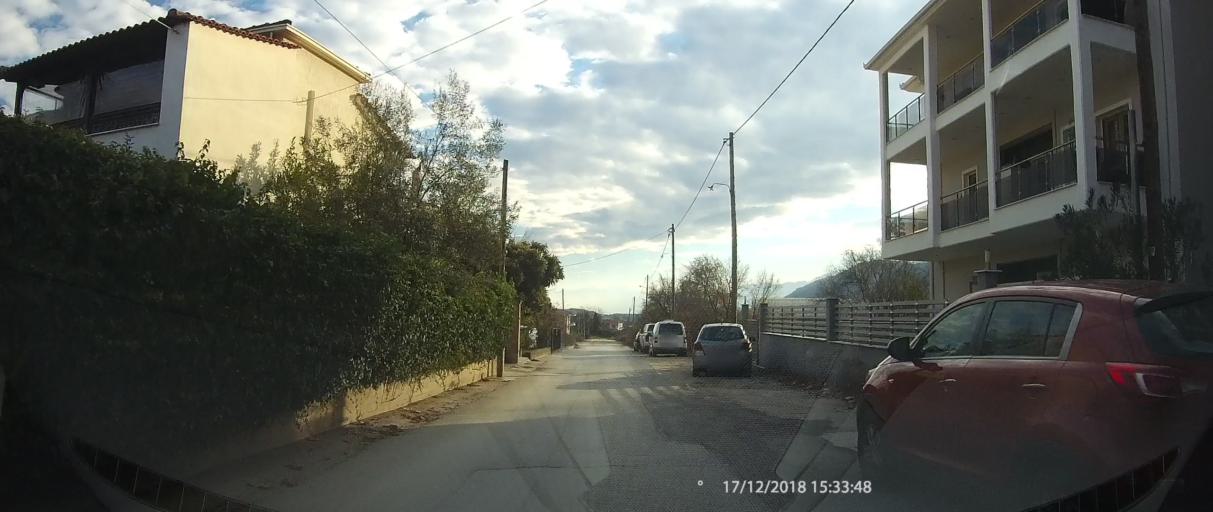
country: GR
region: Thessaly
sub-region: Trikala
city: Kalampaka
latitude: 39.7008
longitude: 21.6329
